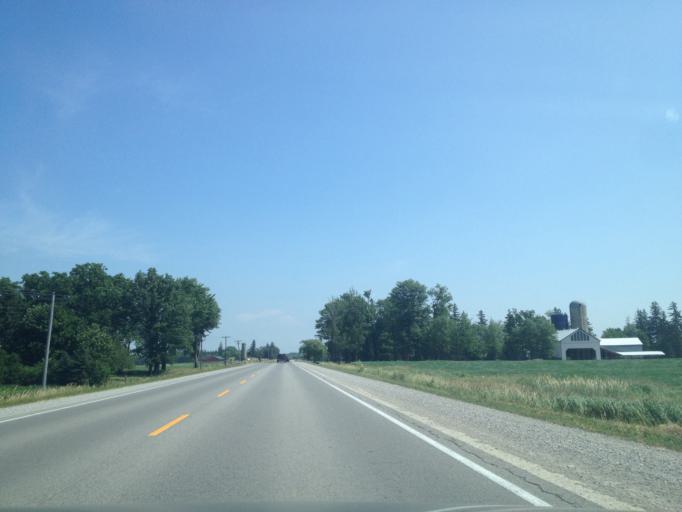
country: CA
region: Ontario
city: Huron East
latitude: 43.4487
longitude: -81.2143
